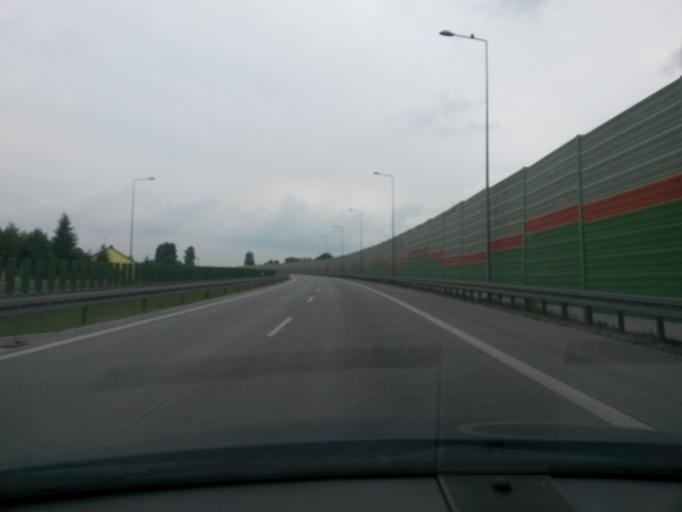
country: PL
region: Lodz Voivodeship
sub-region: Powiat rawski
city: Rawa Mazowiecka
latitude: 51.7460
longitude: 20.2390
